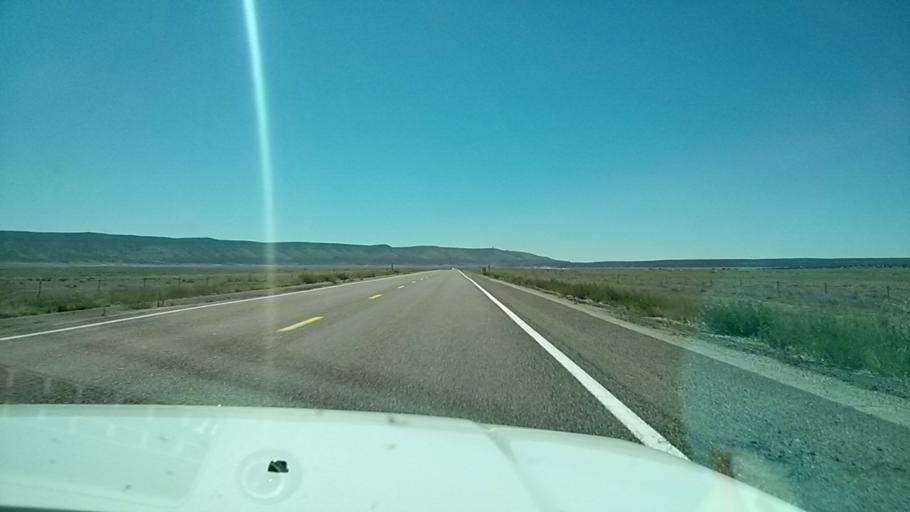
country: US
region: Arizona
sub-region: Mohave County
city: Peach Springs
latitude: 35.4162
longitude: -113.0402
